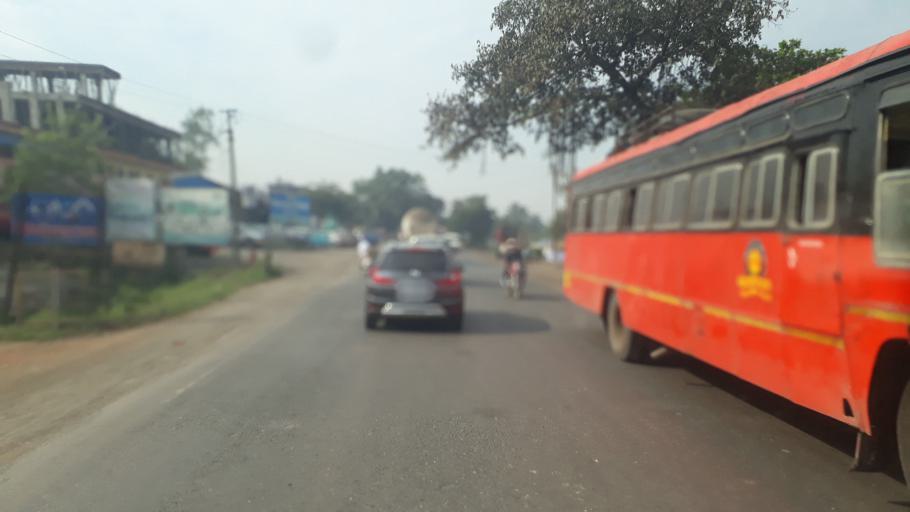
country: IN
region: Maharashtra
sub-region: Raigarh
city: Pen
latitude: 18.7165
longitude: 73.0597
